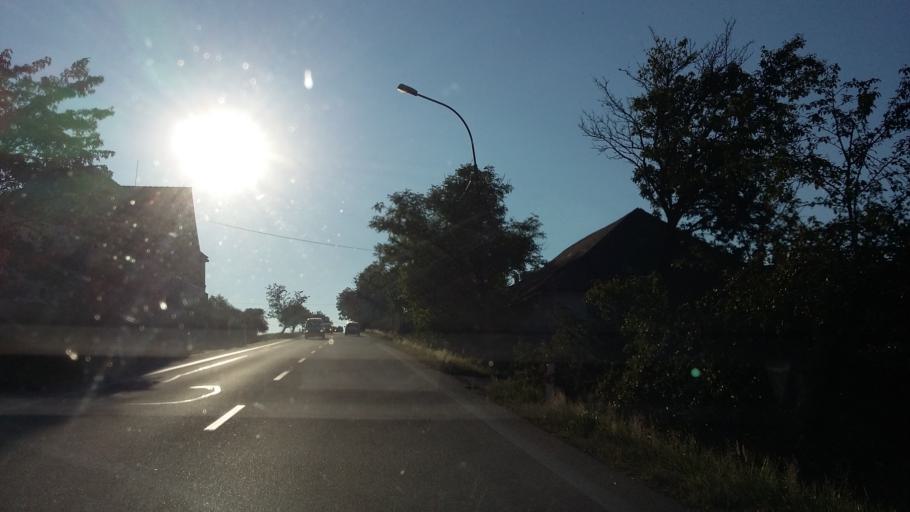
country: CZ
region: Vysocina
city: Velky Beranov
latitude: 49.4016
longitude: 15.6734
